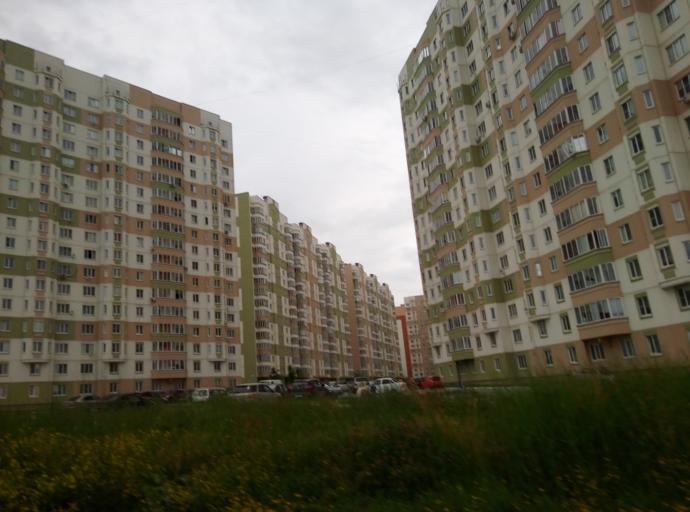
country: RU
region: Kursk
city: Kursk
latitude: 51.7177
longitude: 36.1395
